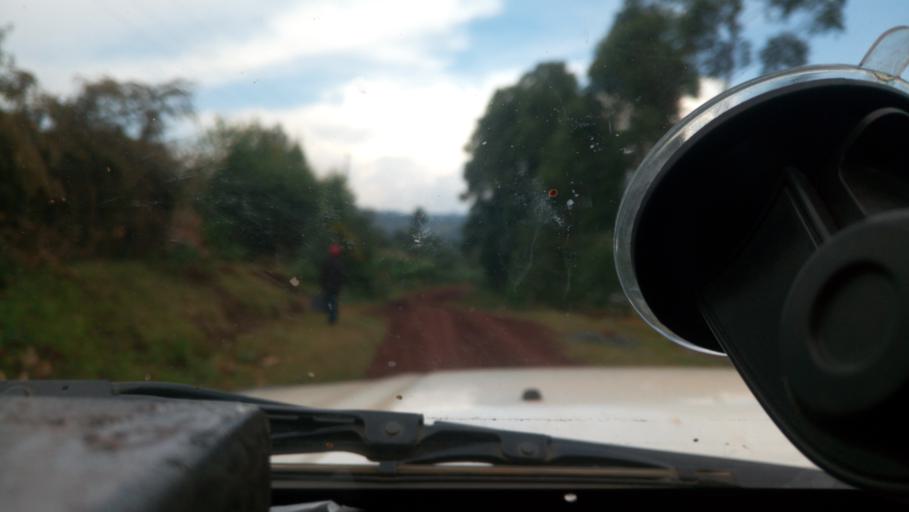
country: KE
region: Kisii
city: Ogembo
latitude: -0.8927
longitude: 34.7862
